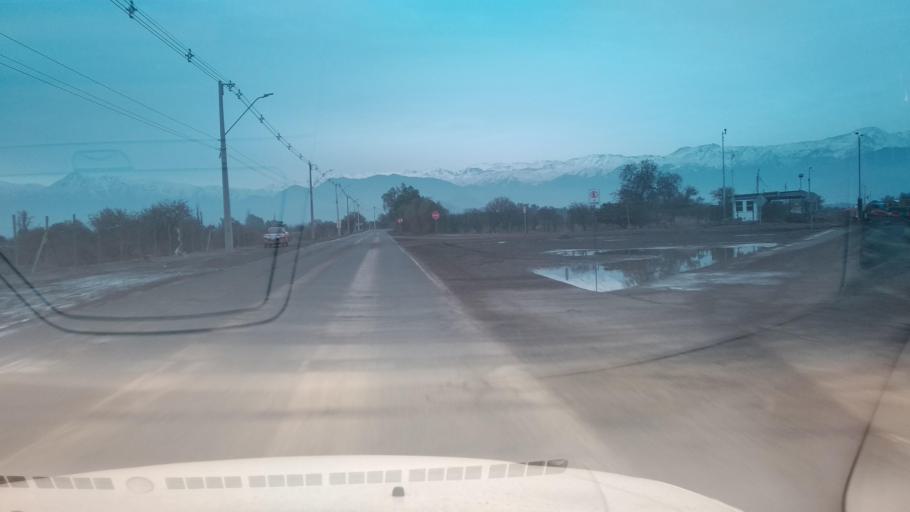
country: CL
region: Santiago Metropolitan
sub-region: Provincia de Chacabuco
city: Chicureo Abajo
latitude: -33.0929
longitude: -70.7419
